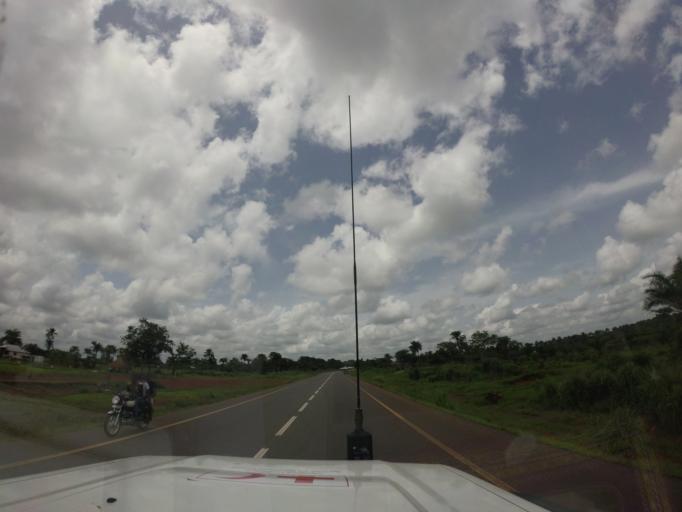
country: SL
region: Northern Province
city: Kambia
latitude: 9.0974
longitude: -12.9139
